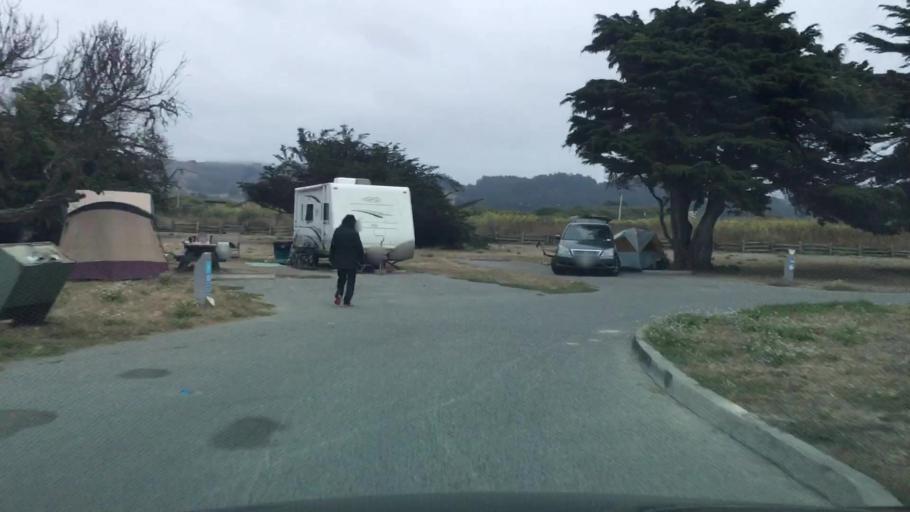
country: US
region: California
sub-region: San Mateo County
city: Half Moon Bay
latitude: 37.4696
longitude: -122.4462
